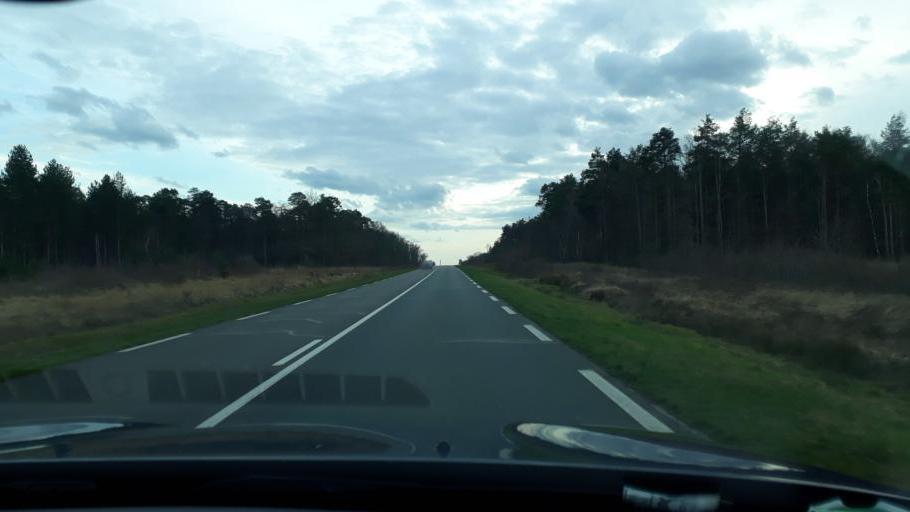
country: FR
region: Centre
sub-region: Departement du Loiret
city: Chilleurs-aux-Bois
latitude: 48.0324
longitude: 2.1193
